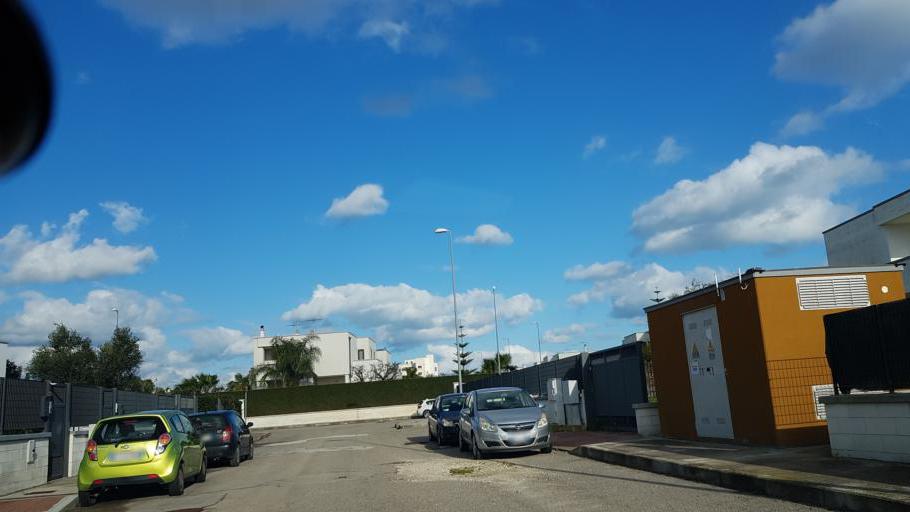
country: IT
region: Apulia
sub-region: Provincia di Brindisi
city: Brindisi
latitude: 40.6418
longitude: 17.9198
